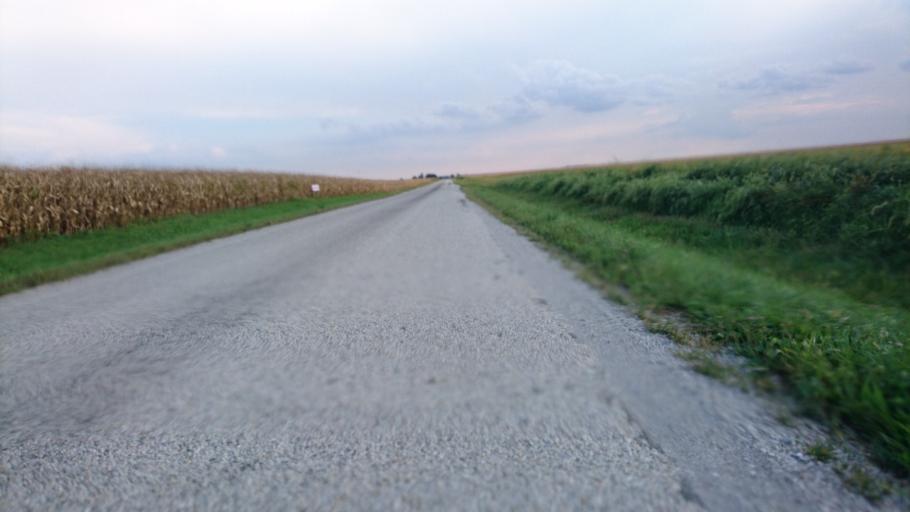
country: US
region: Illinois
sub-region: Logan County
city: Atlanta
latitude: 40.2552
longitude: -89.2052
